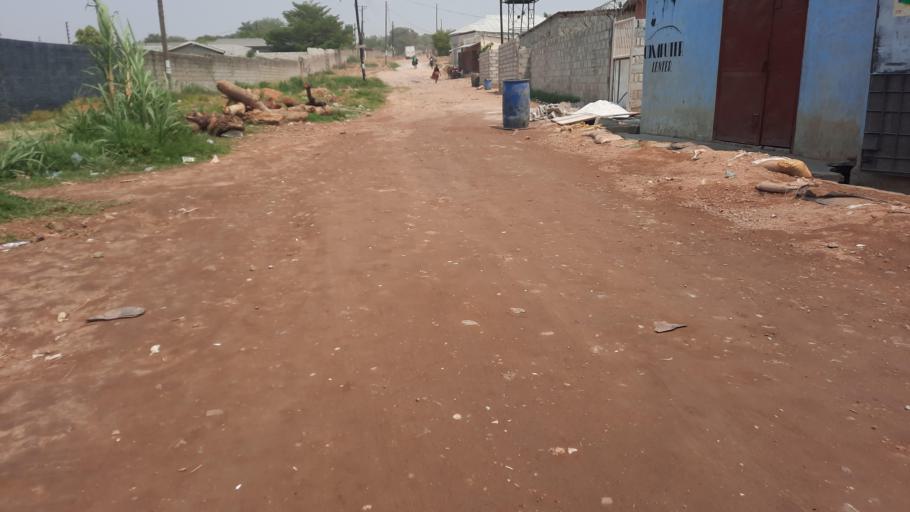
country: ZM
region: Lusaka
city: Lusaka
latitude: -15.4099
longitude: 28.3762
